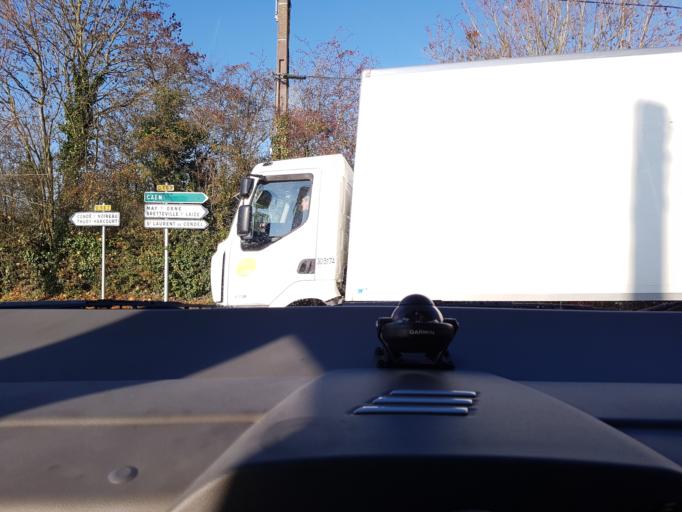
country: FR
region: Lower Normandy
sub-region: Departement du Calvados
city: Thury-Harcourt
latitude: 49.0002
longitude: -0.4403
